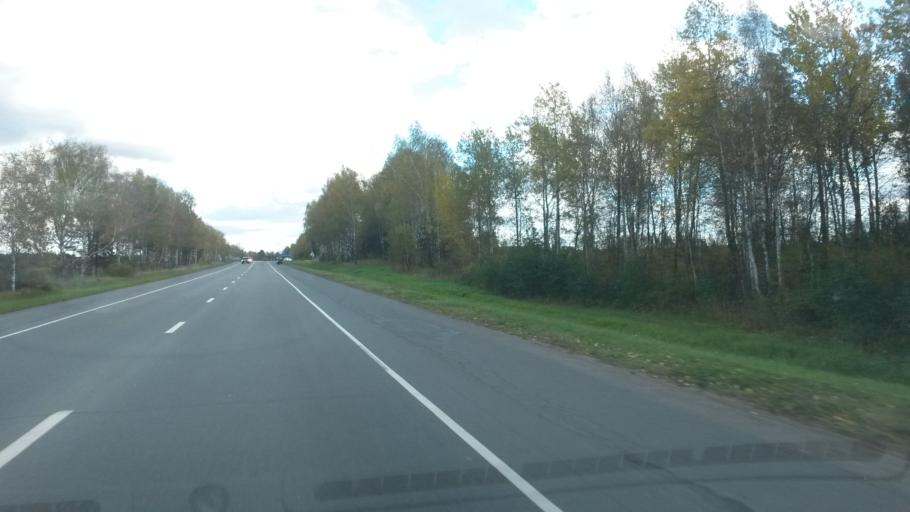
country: RU
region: Jaroslavl
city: Tunoshna
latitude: 57.5371
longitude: 40.0149
